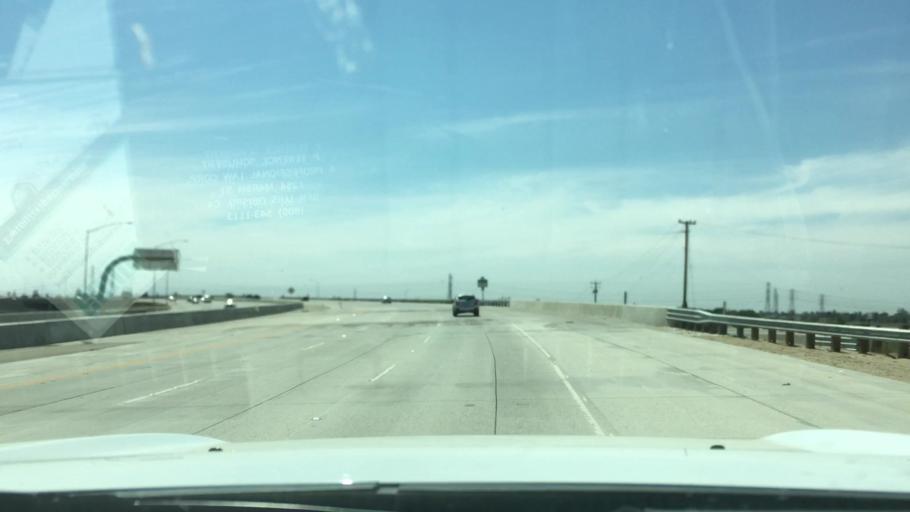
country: US
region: California
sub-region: Kern County
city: Greenacres
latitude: 35.3686
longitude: -119.0867
